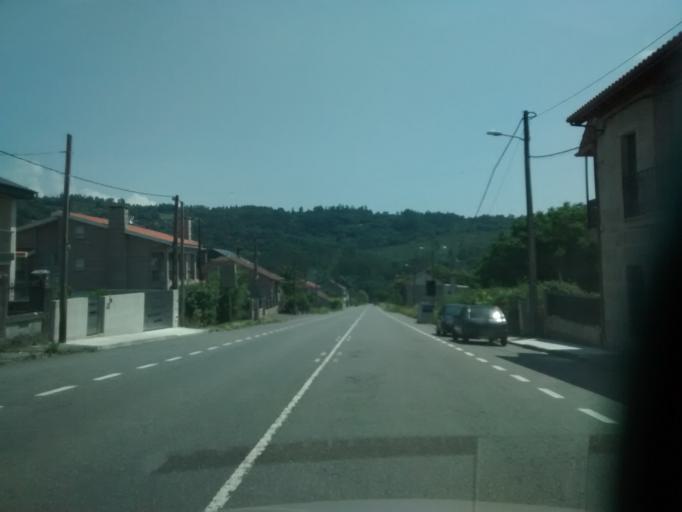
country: ES
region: Galicia
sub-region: Provincia de Ourense
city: Boboras
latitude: 42.4507
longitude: -8.1476
